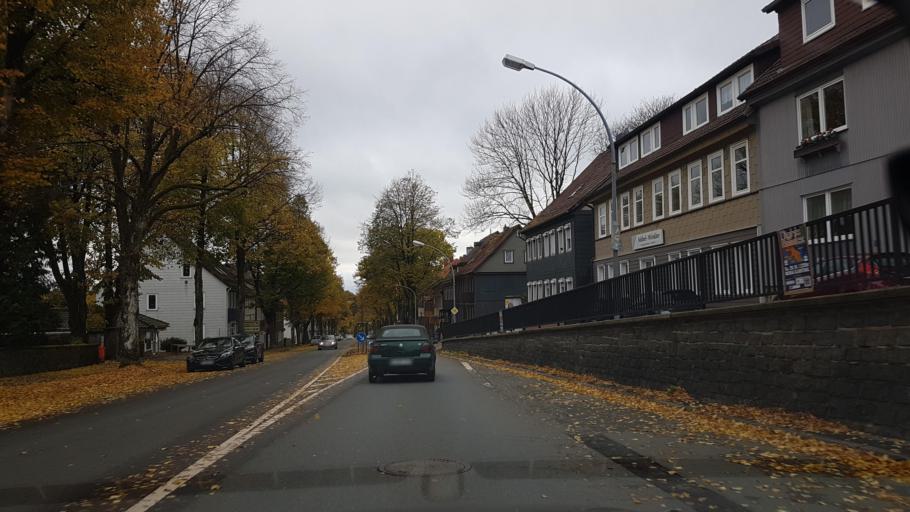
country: DE
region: Lower Saxony
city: Clausthal-Zellerfeld
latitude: 51.8191
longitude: 10.3387
